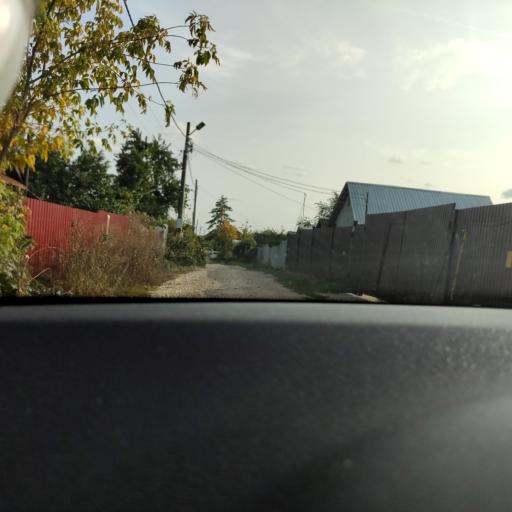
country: RU
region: Samara
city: Petra-Dubrava
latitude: 53.2778
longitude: 50.2964
